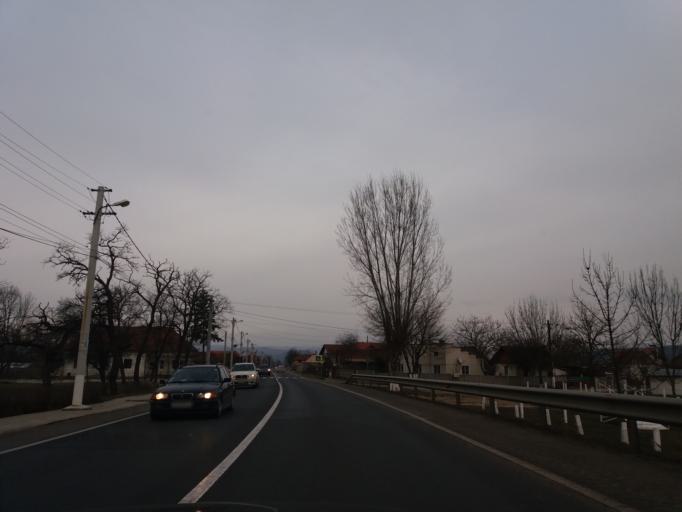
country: RO
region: Hunedoara
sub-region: Comuna Bacia
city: Bacia
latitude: 45.8026
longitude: 23.0120
